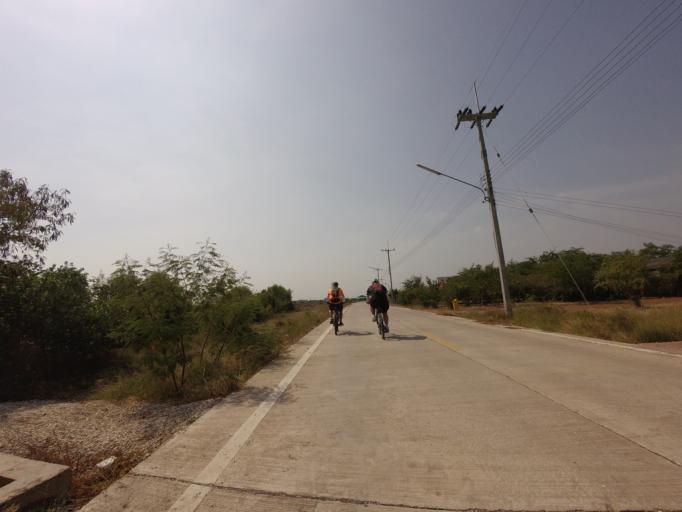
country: TH
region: Samut Sakhon
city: Samut Sakhon
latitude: 13.5136
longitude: 100.3985
